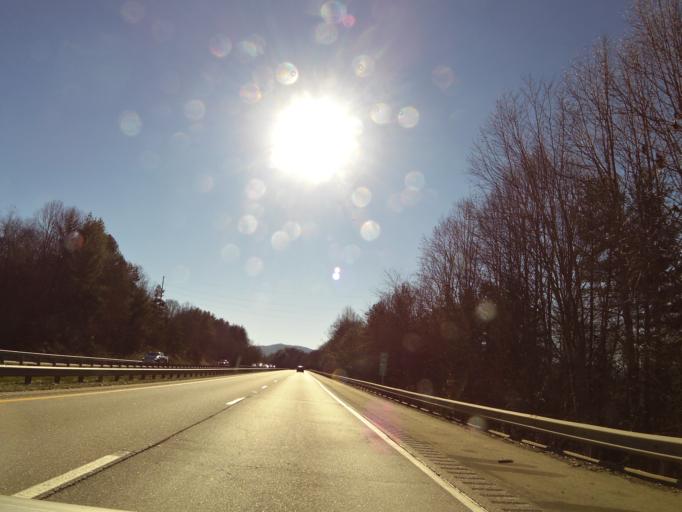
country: US
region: North Carolina
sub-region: Haywood County
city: Lake Junaluska
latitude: 35.5611
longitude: -82.9505
